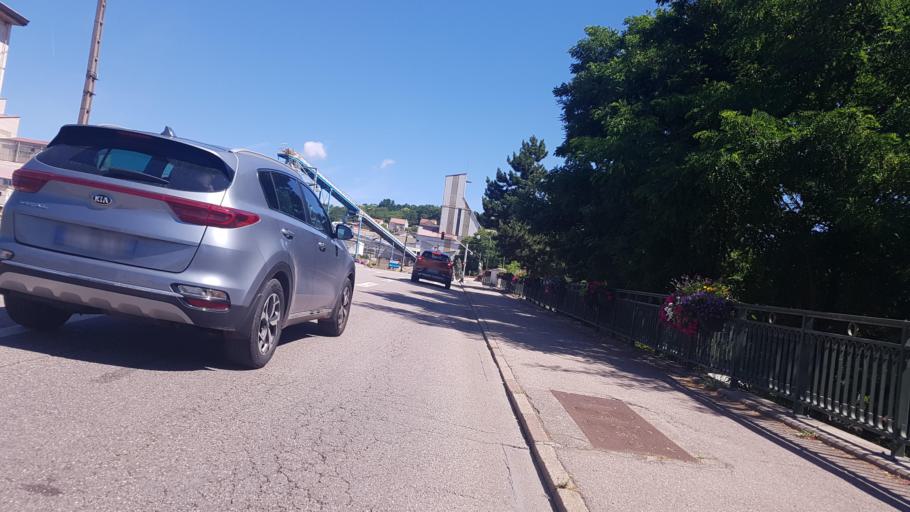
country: FR
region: Lorraine
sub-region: Departement de Meurthe-et-Moselle
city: Varangeville
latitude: 48.6353
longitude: 6.3109
